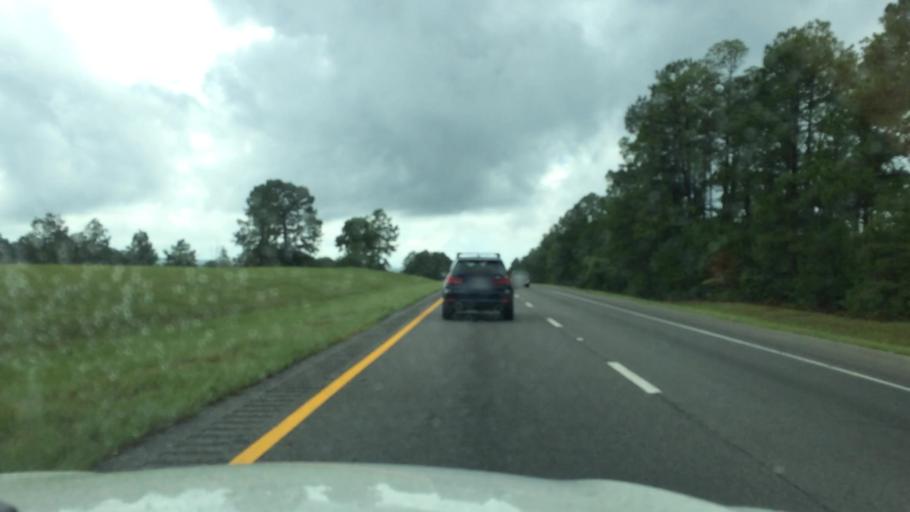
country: US
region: South Carolina
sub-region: Kershaw County
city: Lugoff
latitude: 34.1659
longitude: -80.7180
